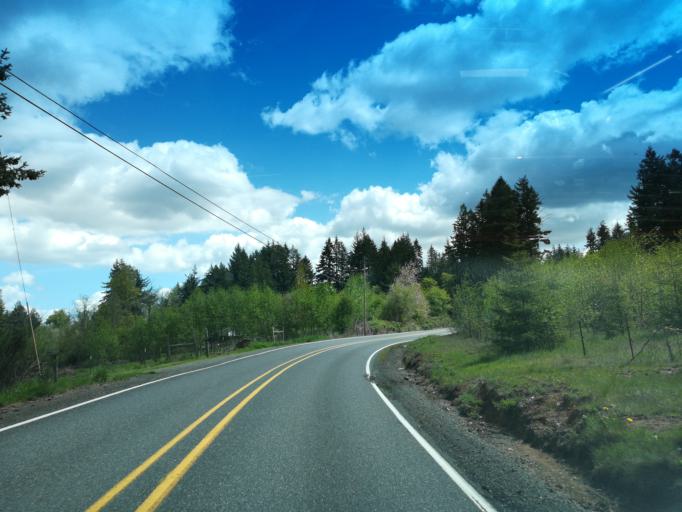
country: US
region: Oregon
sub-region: Clackamas County
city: Damascus
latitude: 45.4401
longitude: -122.4430
